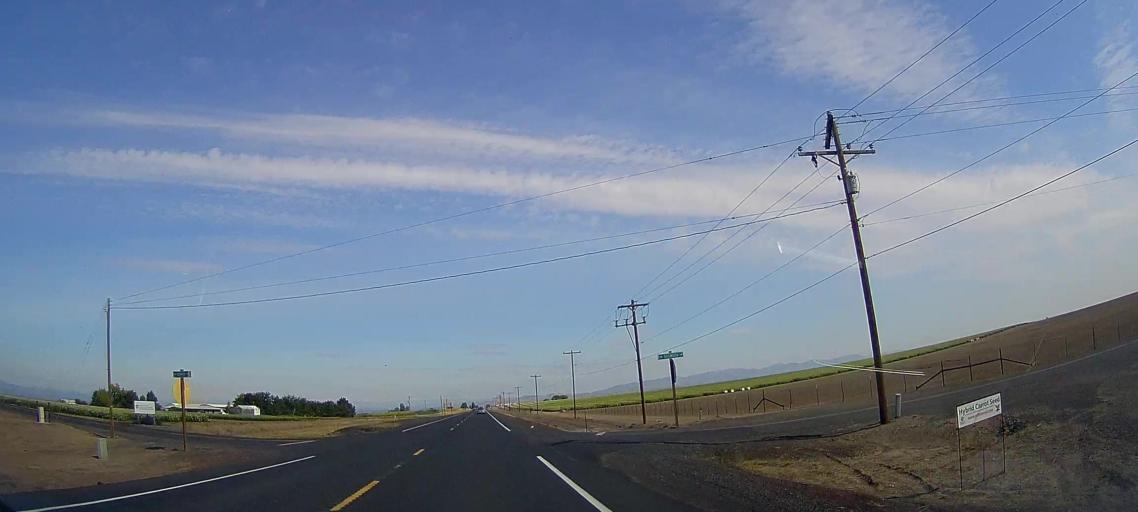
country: US
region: Oregon
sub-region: Jefferson County
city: Madras
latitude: 44.6790
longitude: -121.1462
